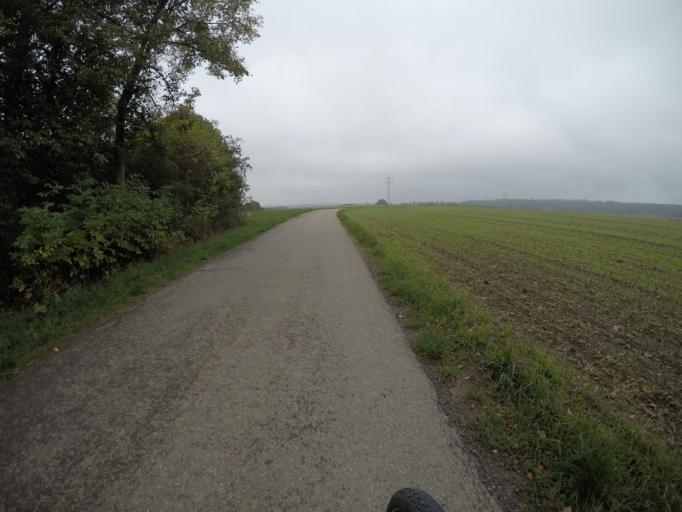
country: DE
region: Baden-Wuerttemberg
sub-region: Regierungsbezirk Stuttgart
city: Gartringen
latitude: 48.6516
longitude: 8.9191
